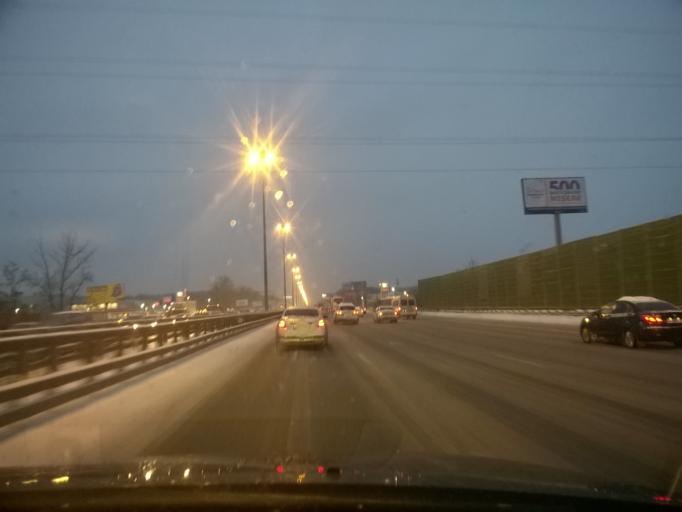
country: RU
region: Moscow
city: Solntsevo
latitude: 55.6181
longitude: 37.3884
